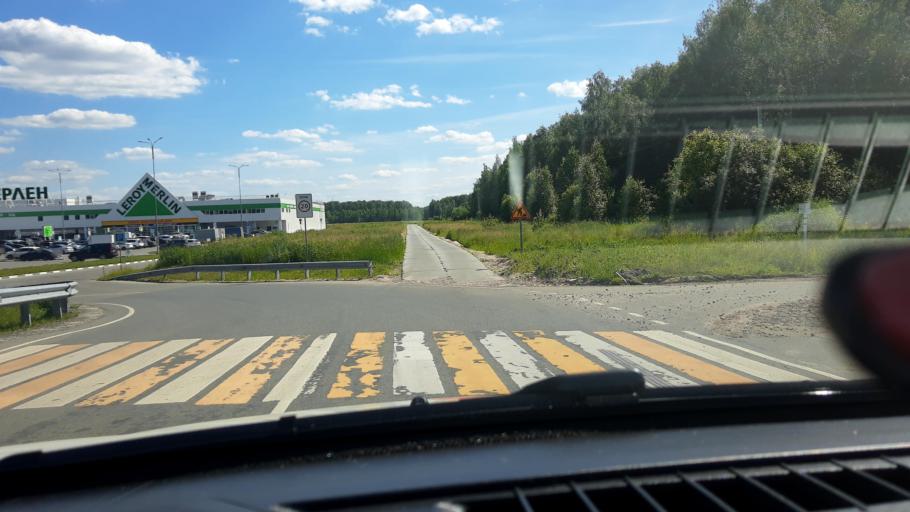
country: RU
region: Nizjnij Novgorod
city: Gorbatovka
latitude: 56.3093
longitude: 43.7696
